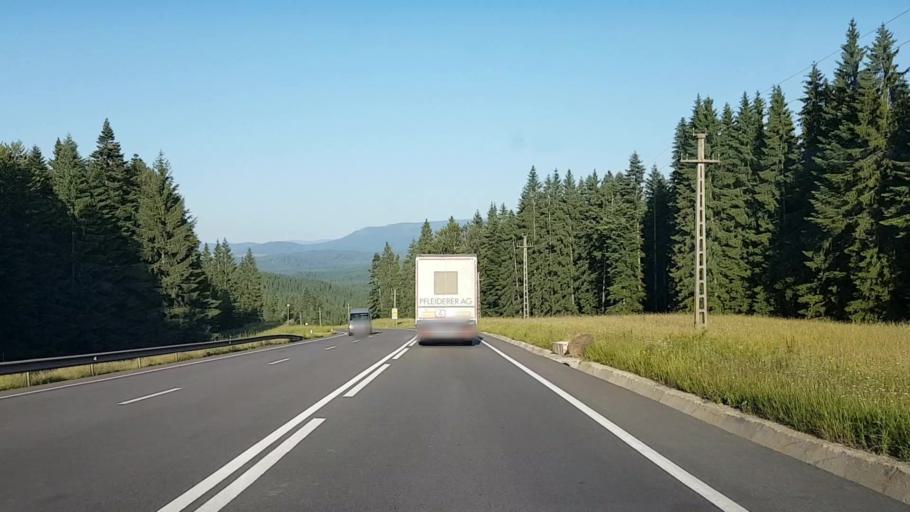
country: RO
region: Suceava
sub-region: Comuna Poiana Stampei
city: Poiana Stampei
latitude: 47.2842
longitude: 25.0470
